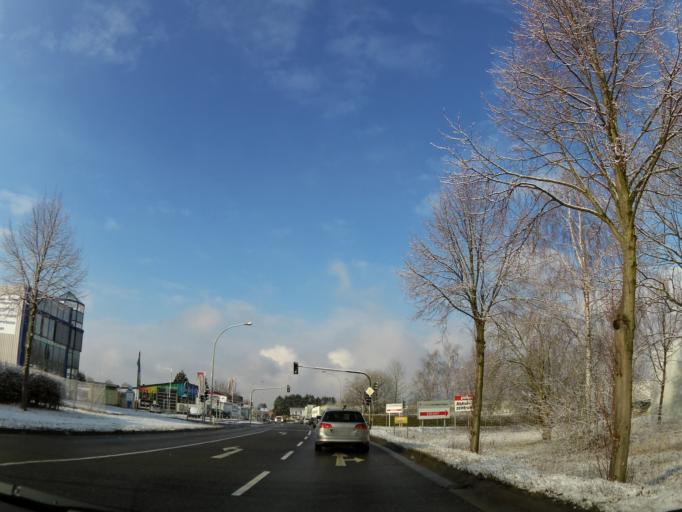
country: DE
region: North Rhine-Westphalia
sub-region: Regierungsbezirk Koln
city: Wurselen
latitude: 50.8310
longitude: 6.1340
